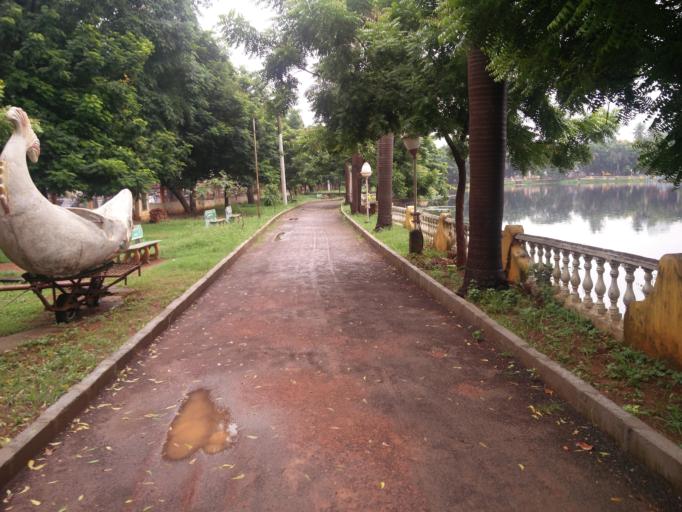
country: IN
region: Andhra Pradesh
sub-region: East Godavari
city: Rajahmundry
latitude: 17.0125
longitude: 81.7785
